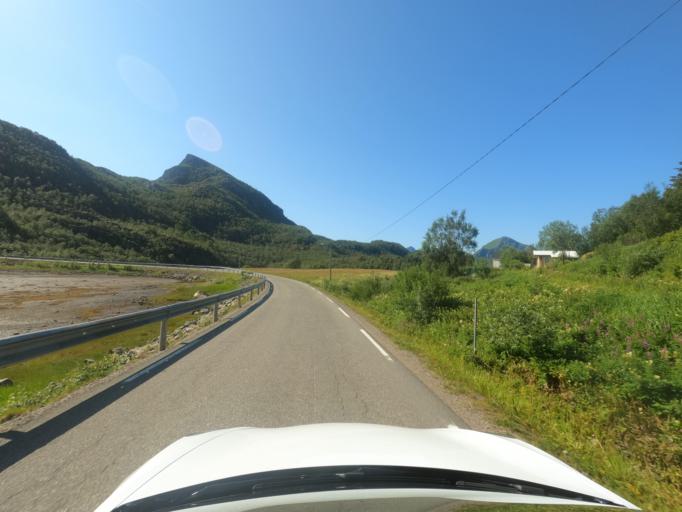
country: NO
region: Nordland
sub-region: Hadsel
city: Stokmarknes
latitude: 68.3005
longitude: 15.0389
